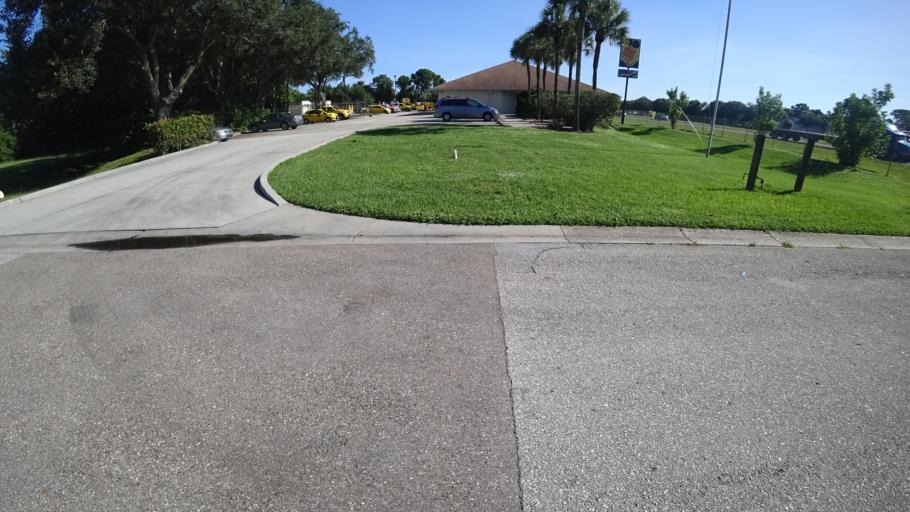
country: US
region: Florida
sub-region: Manatee County
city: Whitfield
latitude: 27.4227
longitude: -82.5328
